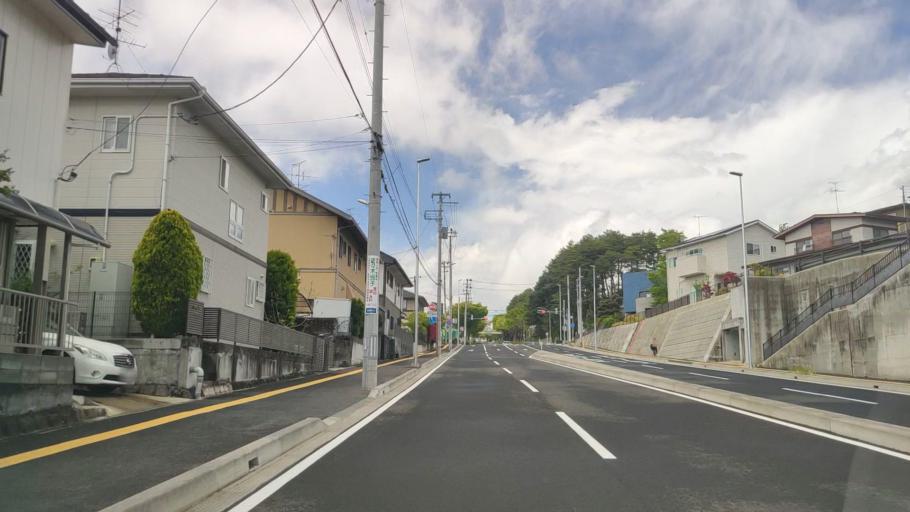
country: JP
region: Miyagi
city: Sendai
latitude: 38.2367
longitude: 140.8506
